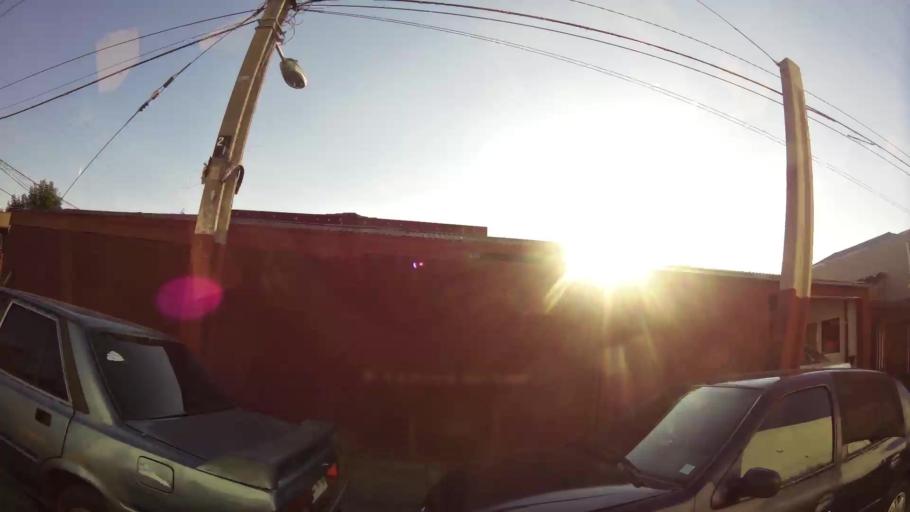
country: CL
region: Santiago Metropolitan
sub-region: Provincia de Santiago
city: La Pintana
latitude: -33.5551
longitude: -70.6184
